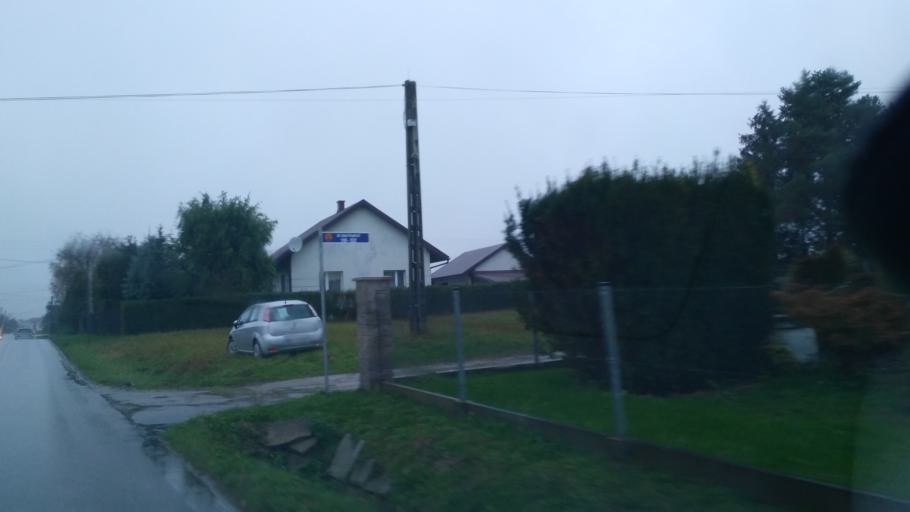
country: PL
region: Subcarpathian Voivodeship
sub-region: Powiat krosnienski
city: Miejsce Piastowe
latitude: 49.6526
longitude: 21.8077
